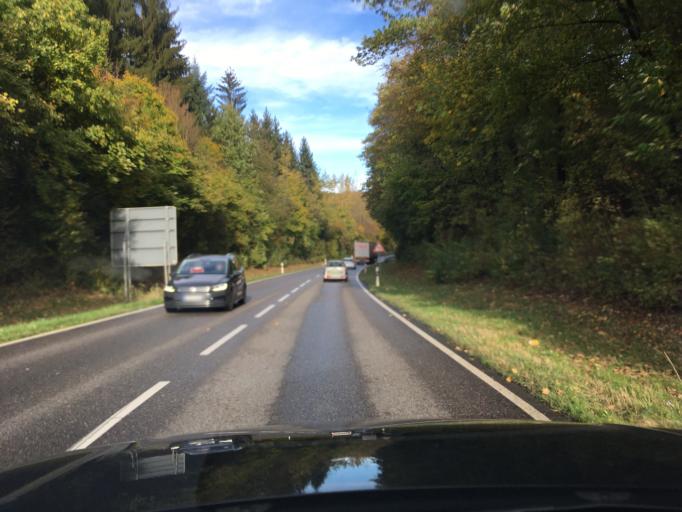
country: DE
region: Baden-Wuerttemberg
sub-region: Regierungsbezirk Stuttgart
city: Mockmuhl
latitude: 49.2840
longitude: 9.3529
